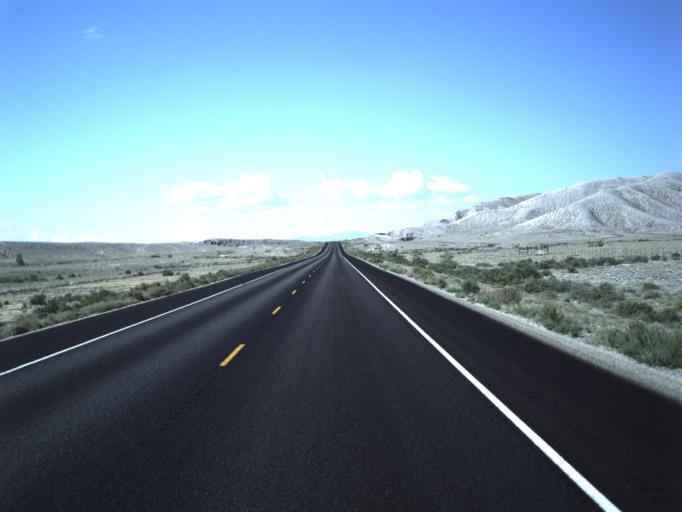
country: US
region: Utah
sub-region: Emery County
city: Ferron
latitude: 39.0174
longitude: -111.1433
